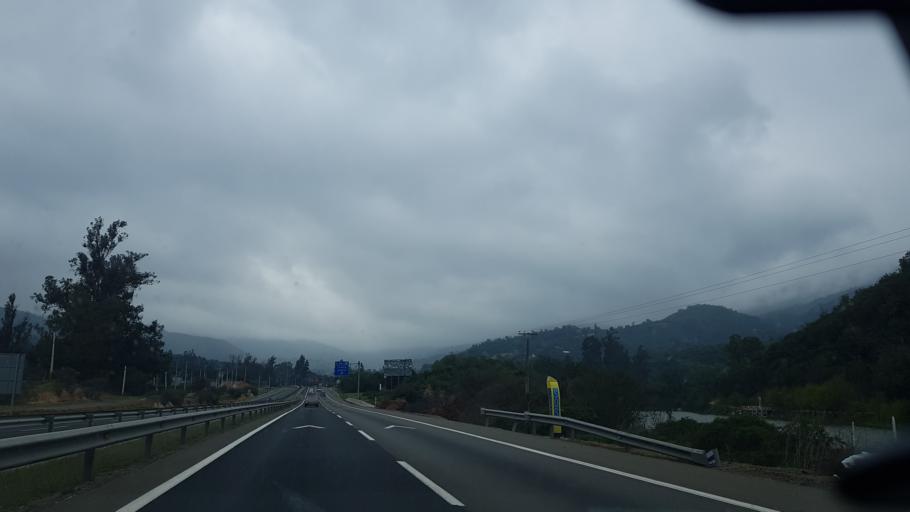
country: CL
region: Santiago Metropolitan
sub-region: Provincia de Melipilla
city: Melipilla
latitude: -33.4044
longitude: -71.2102
